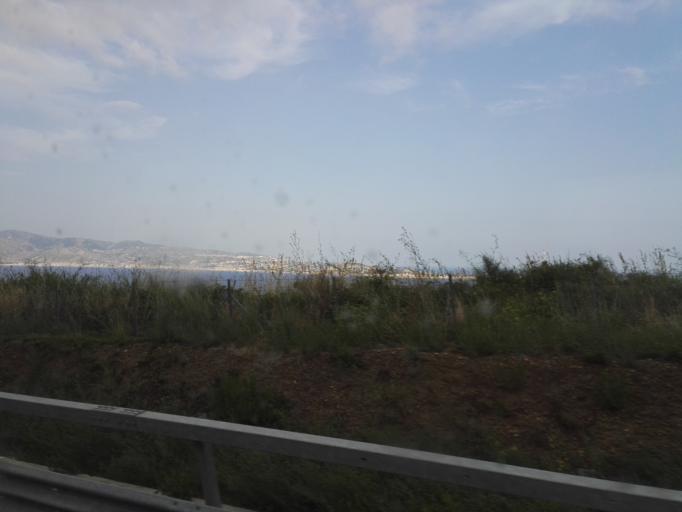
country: IT
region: Calabria
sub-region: Provincia di Reggio Calabria
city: Villa San Giovanni
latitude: 38.2366
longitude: 15.6768
